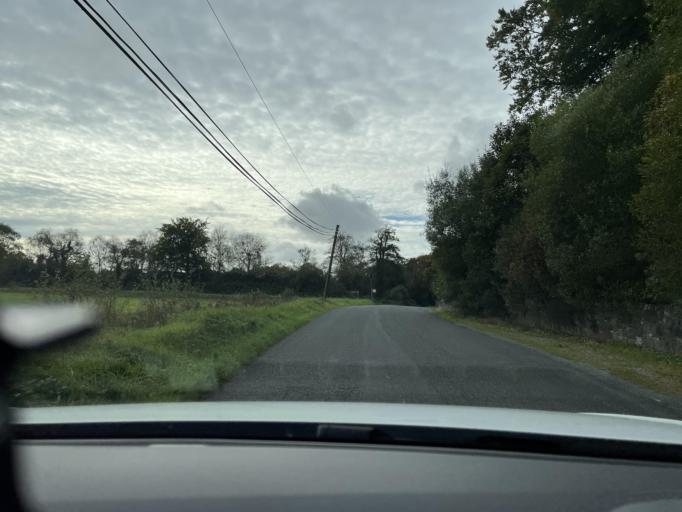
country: IE
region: Connaught
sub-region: Roscommon
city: Boyle
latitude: 54.0197
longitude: -8.3572
